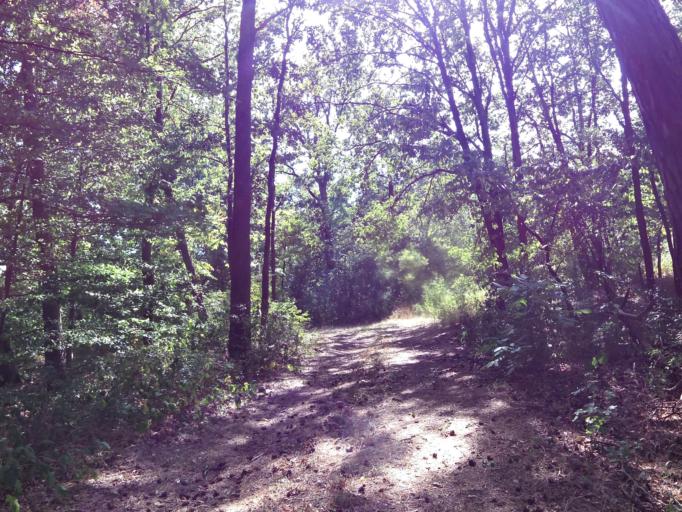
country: DE
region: Bavaria
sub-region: Regierungsbezirk Unterfranken
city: Eibelstadt
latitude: 49.7448
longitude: 10.0096
